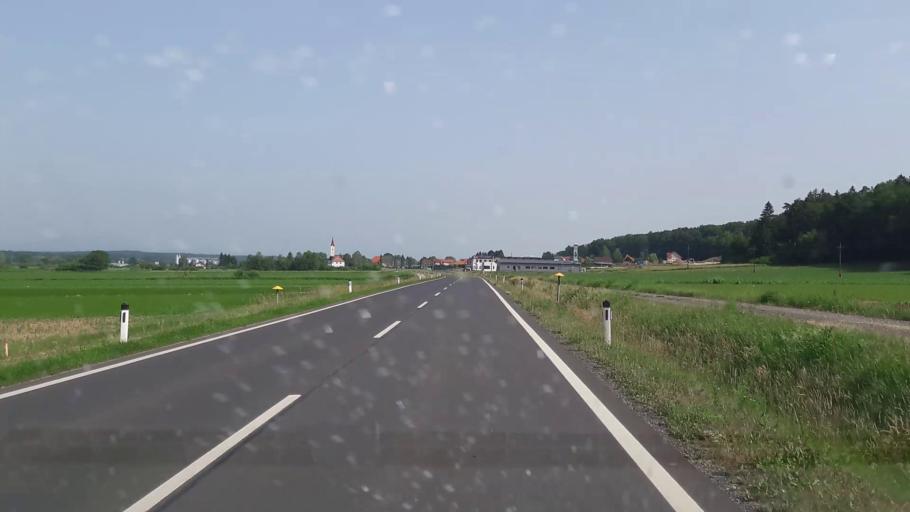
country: AT
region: Burgenland
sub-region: Politischer Bezirk Jennersdorf
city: Deutsch Kaltenbrunn
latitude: 47.0733
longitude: 16.1125
